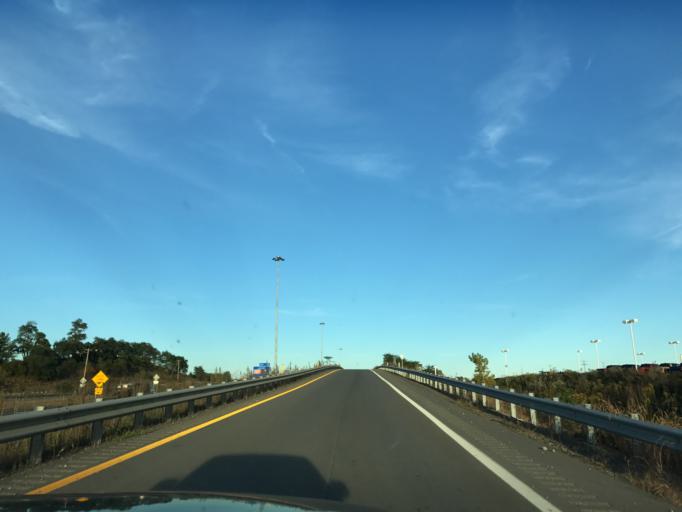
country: US
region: West Virginia
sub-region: Ohio County
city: Bethlehem
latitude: 40.0637
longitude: -80.5878
